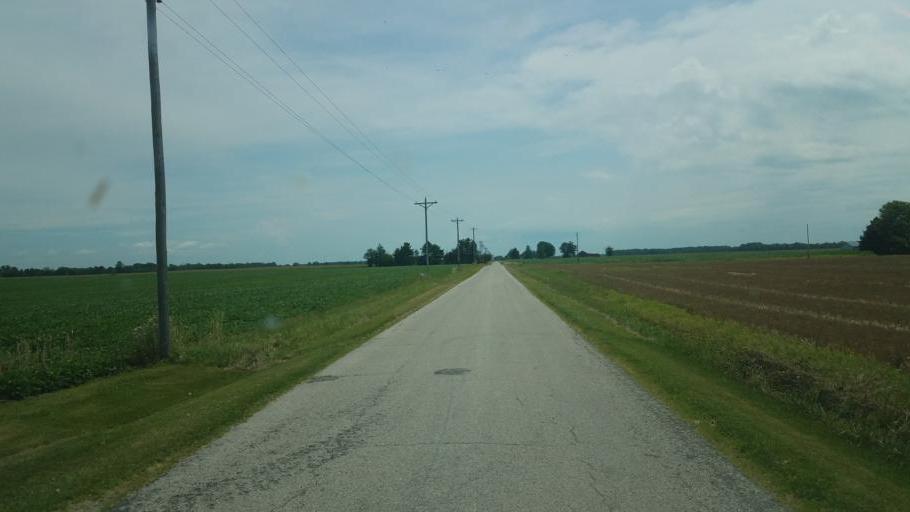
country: US
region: Ohio
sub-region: Crawford County
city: Bucyrus
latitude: 40.8776
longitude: -83.0480
